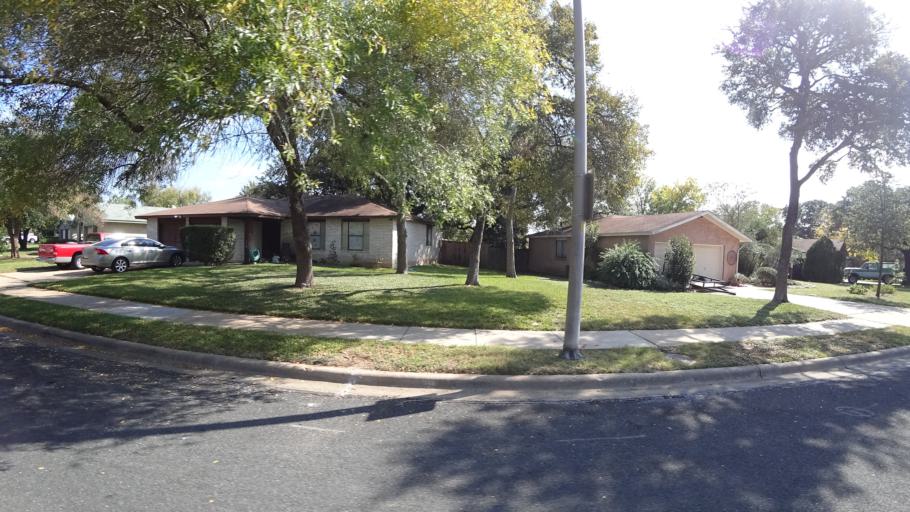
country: US
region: Texas
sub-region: Travis County
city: Rollingwood
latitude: 30.2150
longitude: -97.8161
